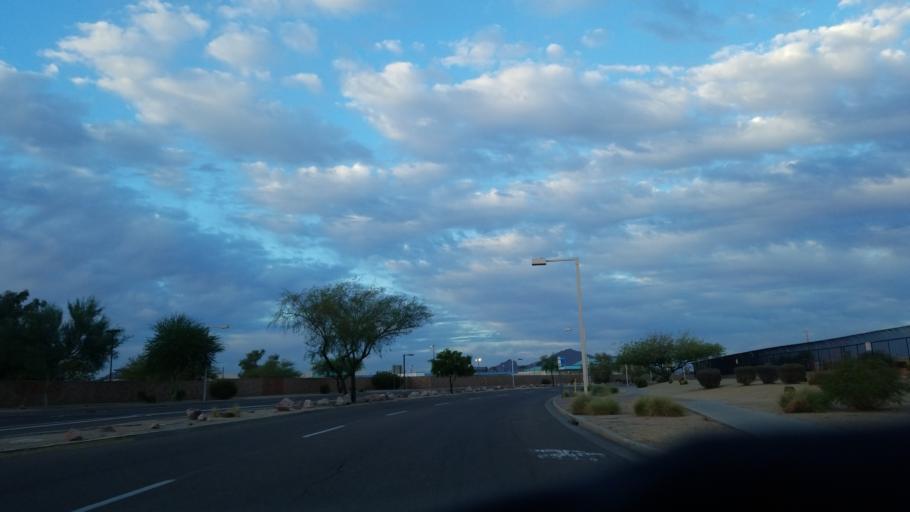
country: US
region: Arizona
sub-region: Maricopa County
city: Phoenix
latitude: 33.4411
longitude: -112.0342
